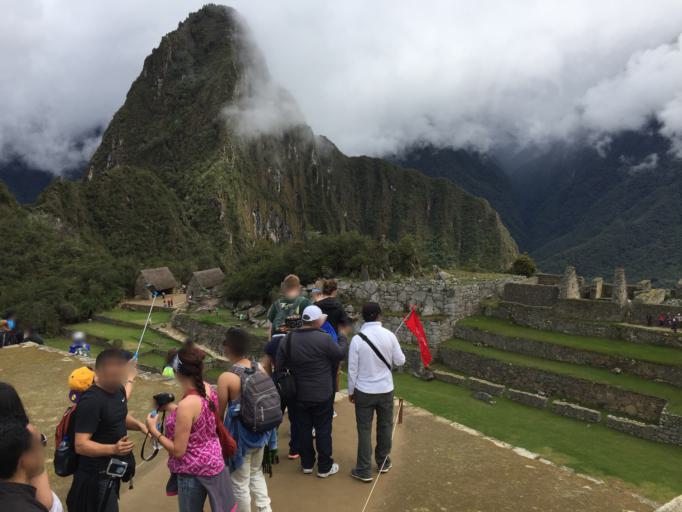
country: PE
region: Cusco
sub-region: Provincia de La Convencion
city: Santa Teresa
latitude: -13.1631
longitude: -72.5457
